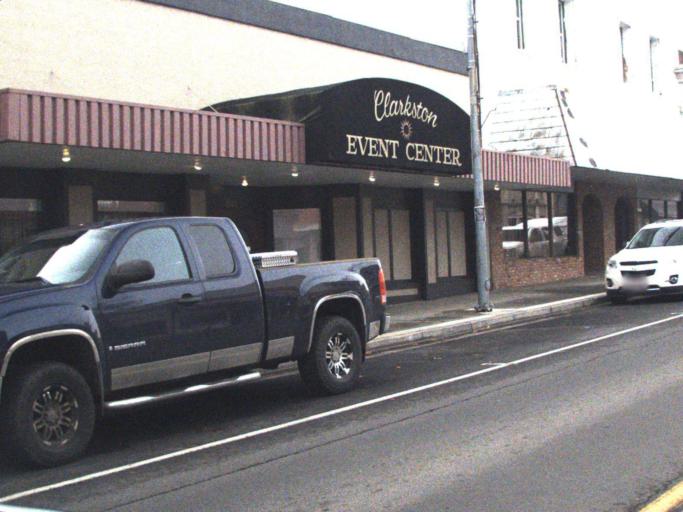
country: US
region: Washington
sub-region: Asotin County
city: Clarkston
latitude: 46.4129
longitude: -117.0456
